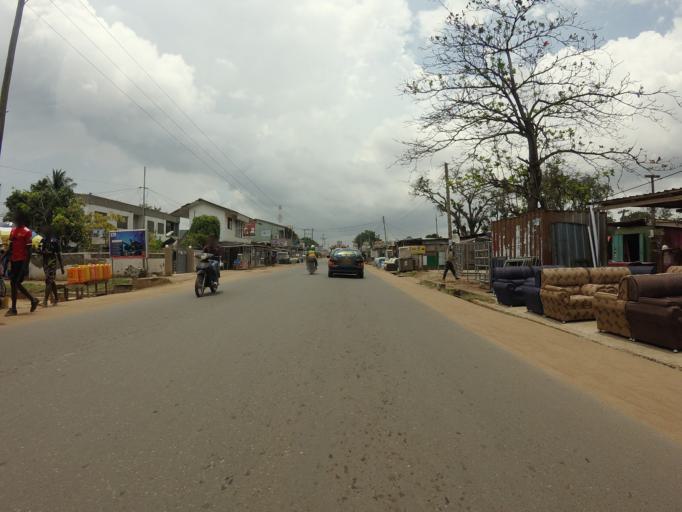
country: GH
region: Greater Accra
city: Medina Estates
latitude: 5.6863
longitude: -0.1663
